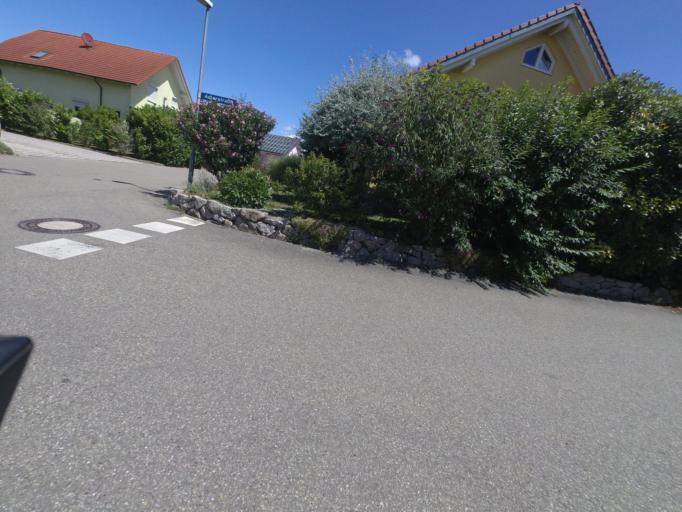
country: DE
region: Baden-Wuerttemberg
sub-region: Karlsruhe Region
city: Ottenhofen
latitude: 48.7564
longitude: 8.1025
